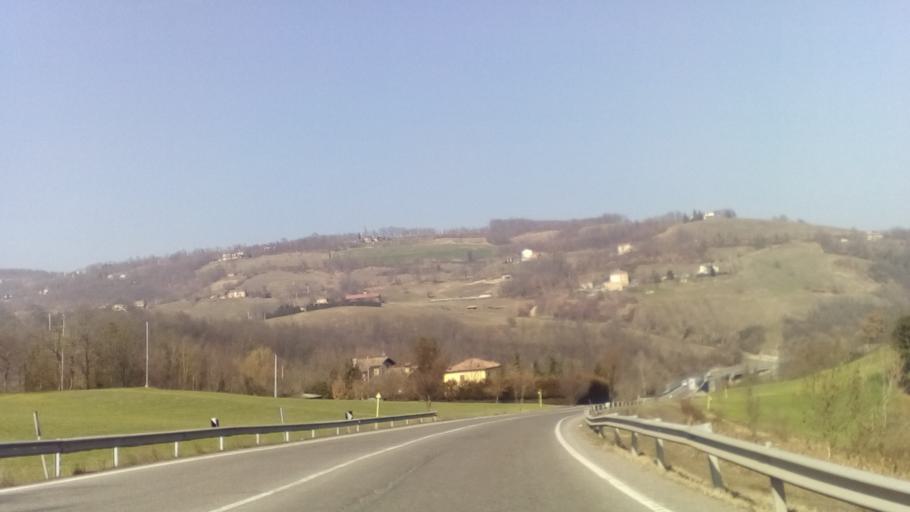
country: IT
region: Emilia-Romagna
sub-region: Provincia di Modena
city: Sant'Antonio
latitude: 44.4001
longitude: 10.8213
